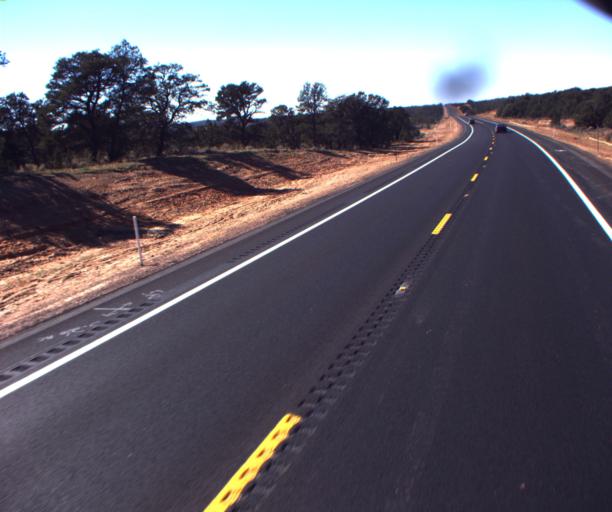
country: US
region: Arizona
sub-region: Apache County
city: Ganado
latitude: 35.7154
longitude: -109.3402
